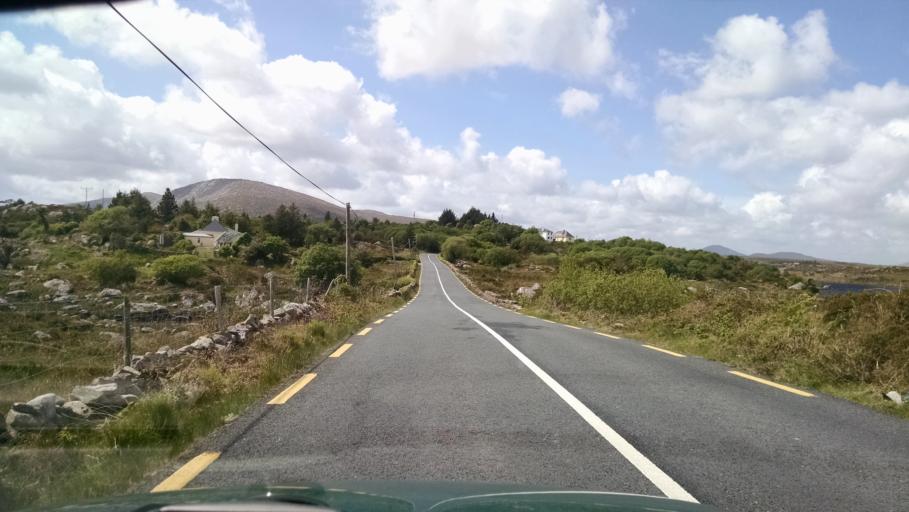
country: IE
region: Connaught
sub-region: County Galway
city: Oughterard
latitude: 53.3910
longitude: -9.6375
